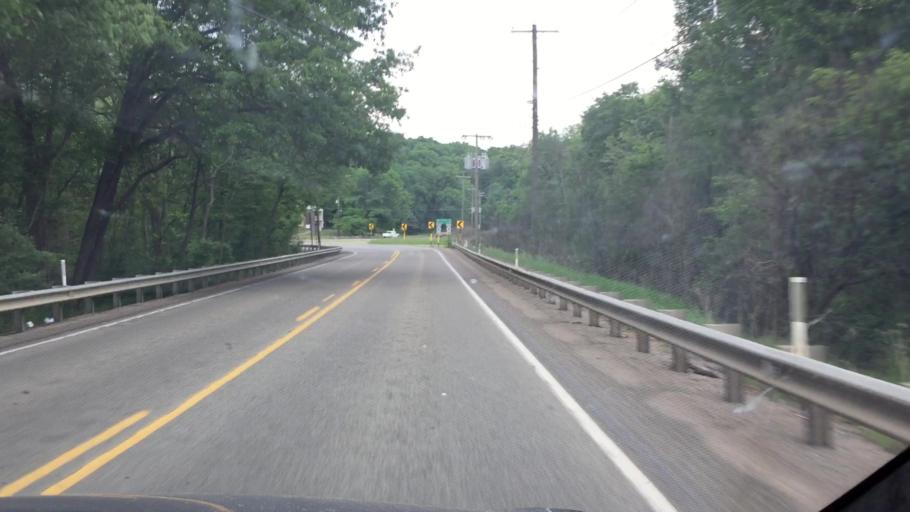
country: US
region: Pennsylvania
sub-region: Butler County
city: Slippery Rock
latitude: 41.0130
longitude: -80.0047
